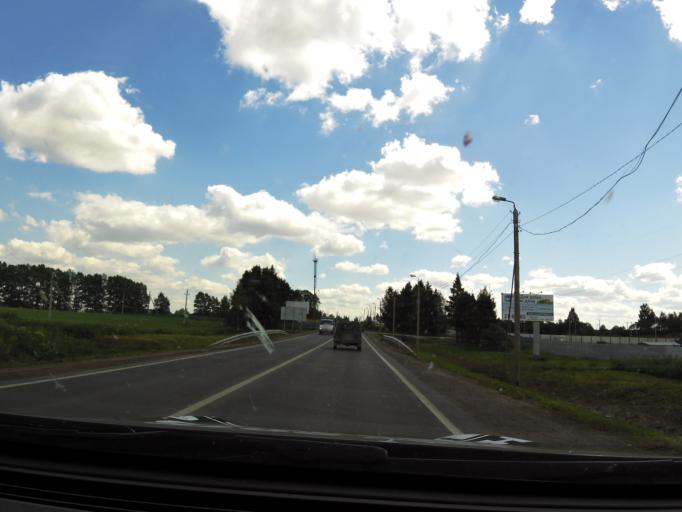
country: RU
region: Vologda
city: Vologda
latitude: 59.2439
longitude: 39.7833
